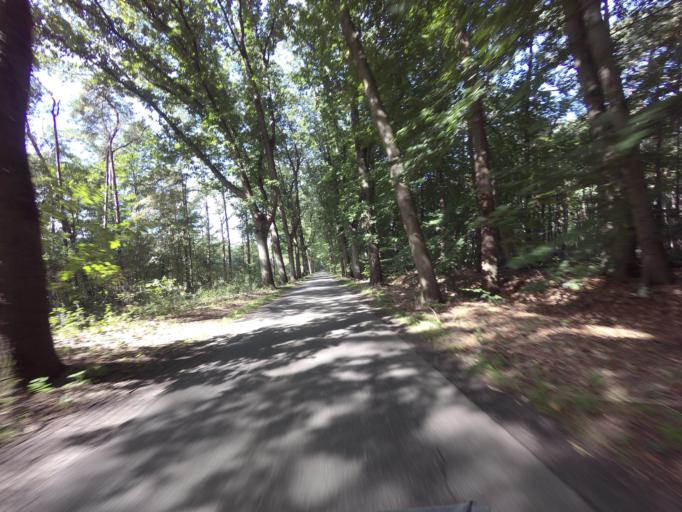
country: NL
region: Overijssel
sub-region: Gemeente Deventer
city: Schalkhaar
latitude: 52.3066
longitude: 6.2122
